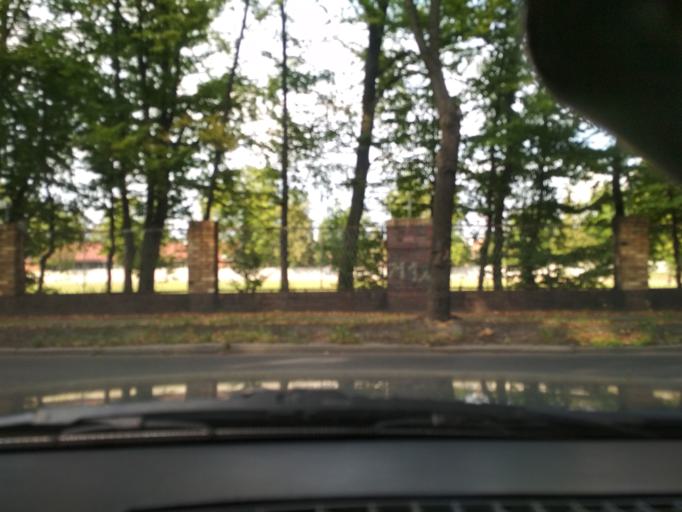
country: PL
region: Silesian Voivodeship
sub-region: Gliwice
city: Gliwice
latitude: 50.2960
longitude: 18.6381
